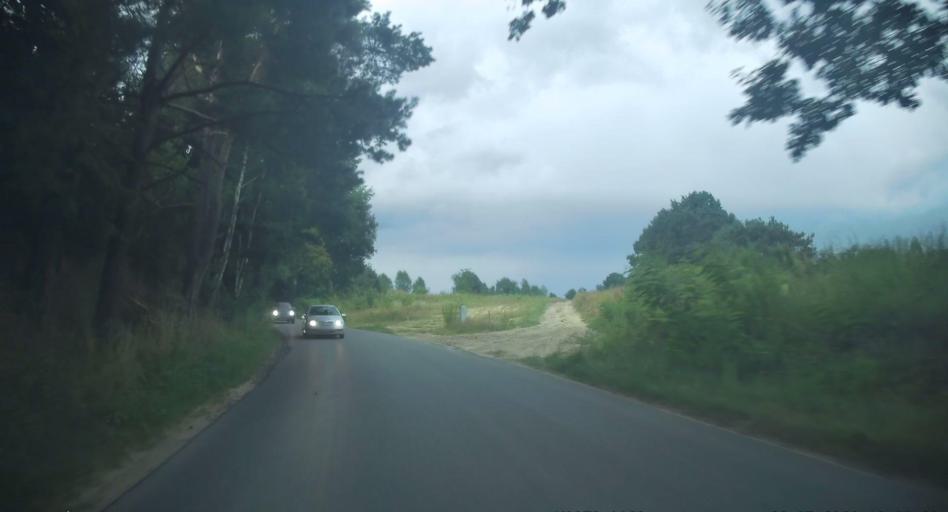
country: PL
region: Lodz Voivodeship
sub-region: Powiat rawski
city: Rawa Mazowiecka
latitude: 51.7431
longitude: 20.2029
